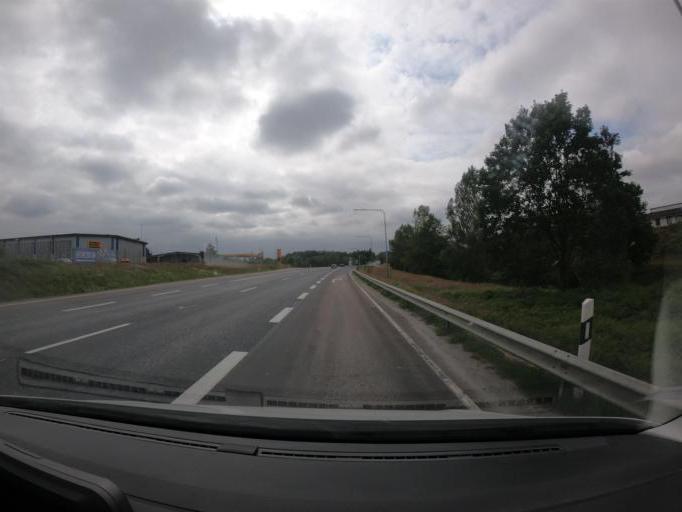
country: SE
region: Skane
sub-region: Orkelljunga Kommun
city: OErkelljunga
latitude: 56.2887
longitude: 13.3050
